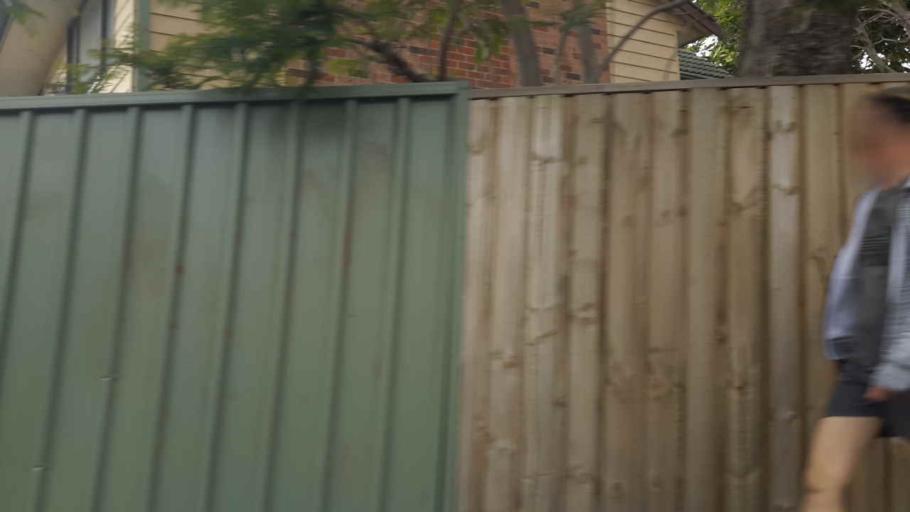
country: AU
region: New South Wales
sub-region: Wollongong
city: Bulli
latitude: -34.3418
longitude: 150.9070
